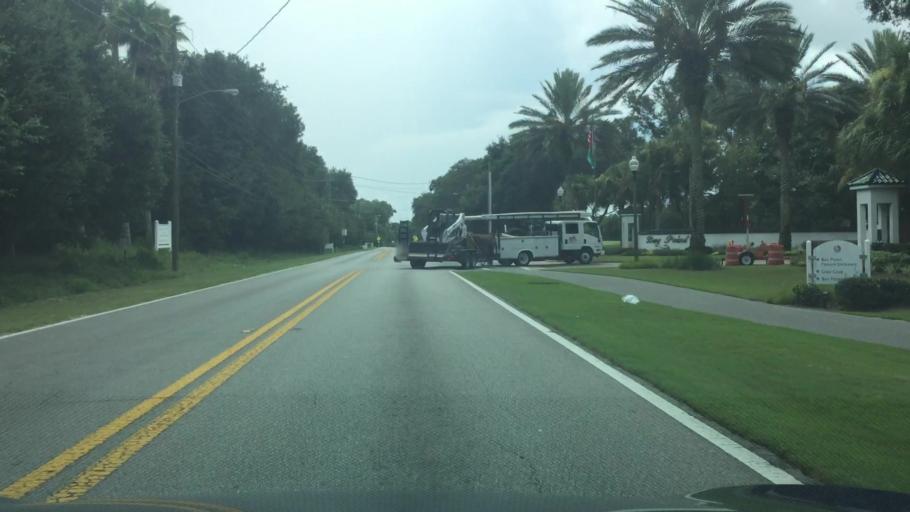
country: US
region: Florida
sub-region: Bay County
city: Upper Grand Lagoon
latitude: 30.1540
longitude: -85.7279
